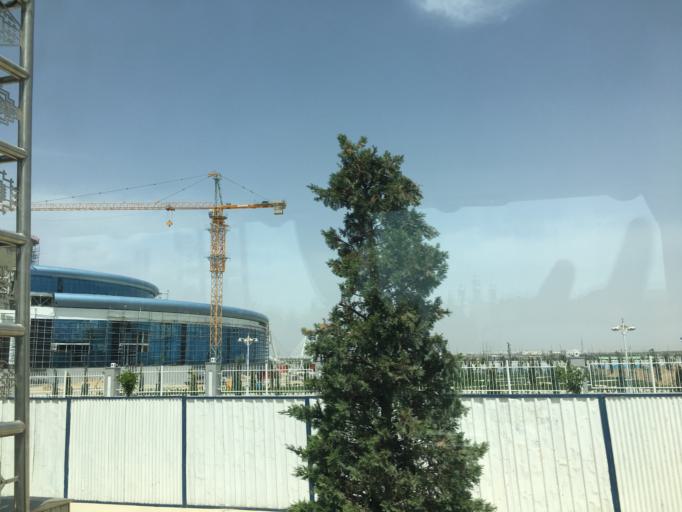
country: TM
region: Balkan
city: Turkmenbasy
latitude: 39.9598
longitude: 52.8443
